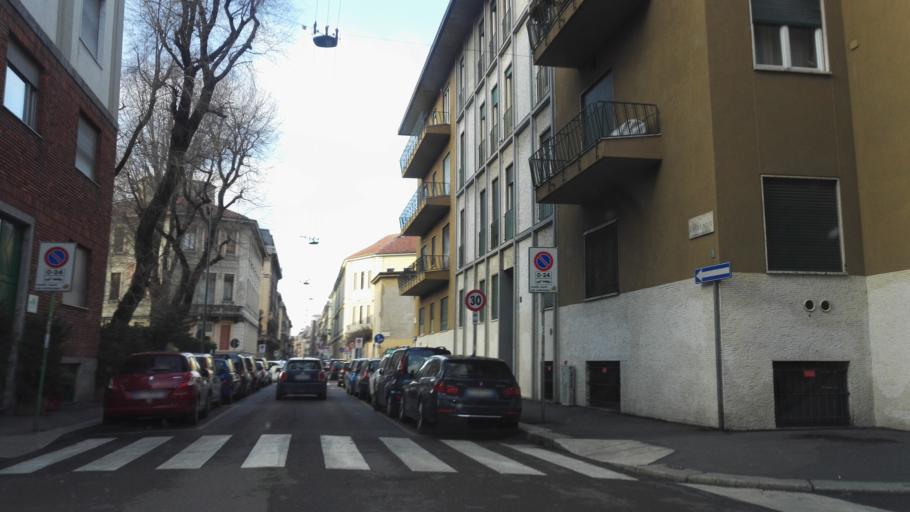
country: IT
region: Lombardy
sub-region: Citta metropolitana di Milano
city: Milano
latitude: 45.4577
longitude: 9.1748
